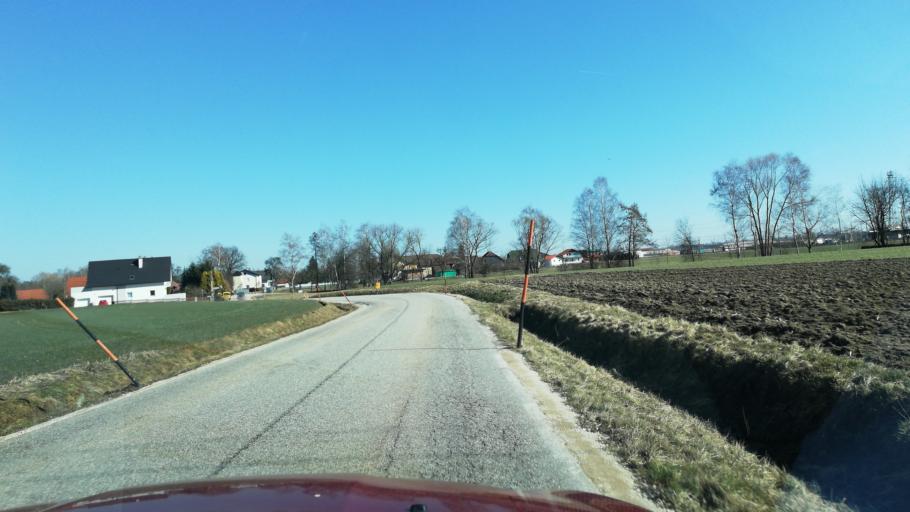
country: AT
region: Upper Austria
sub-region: Politischer Bezirk Vocklabruck
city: Redlham
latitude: 48.0251
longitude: 13.7275
